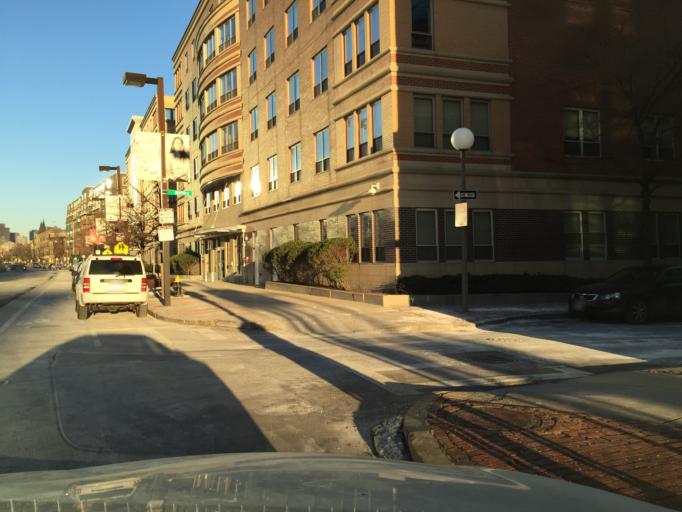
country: US
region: Massachusetts
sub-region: Suffolk County
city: Boston
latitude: 42.3379
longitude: -71.0852
